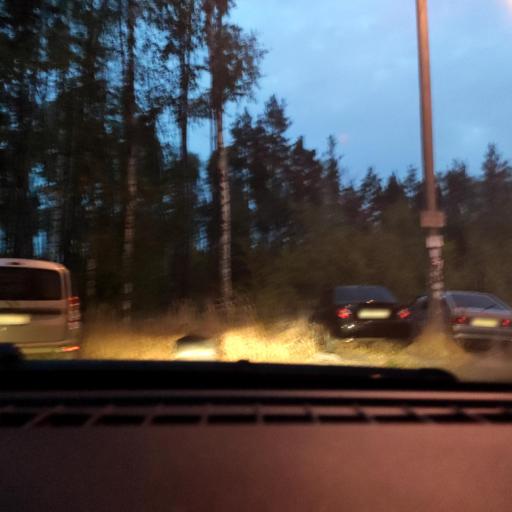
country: RU
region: Voronezj
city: Voronezh
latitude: 51.6943
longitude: 39.2795
